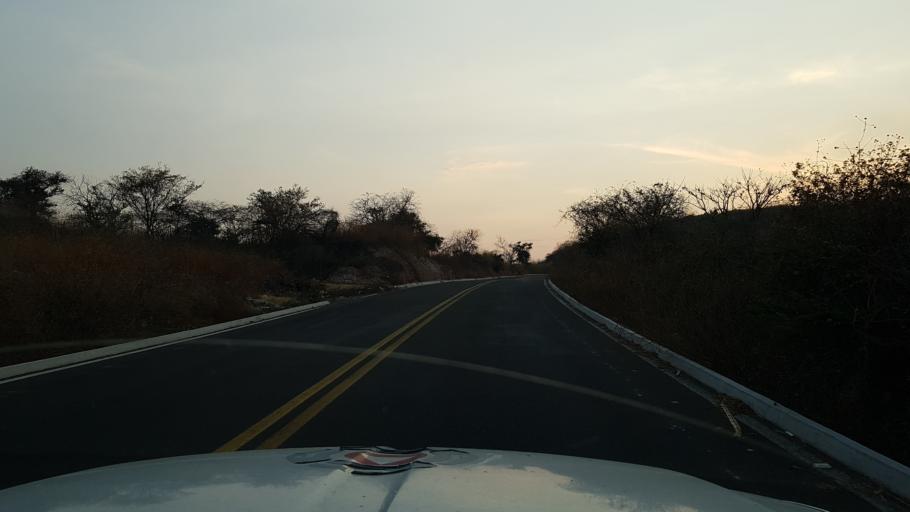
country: MX
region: Morelos
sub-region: Ayala
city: Olintepec
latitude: 18.7333
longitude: -99.0153
